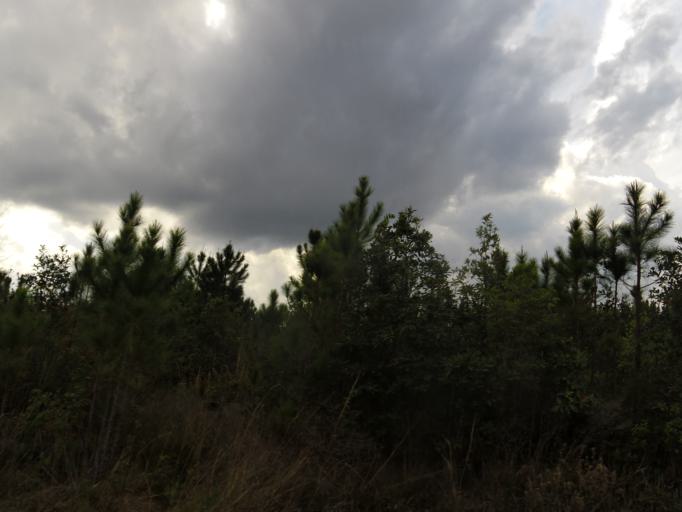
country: US
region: Georgia
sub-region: Charlton County
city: Folkston
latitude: 30.8169
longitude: -82.0706
